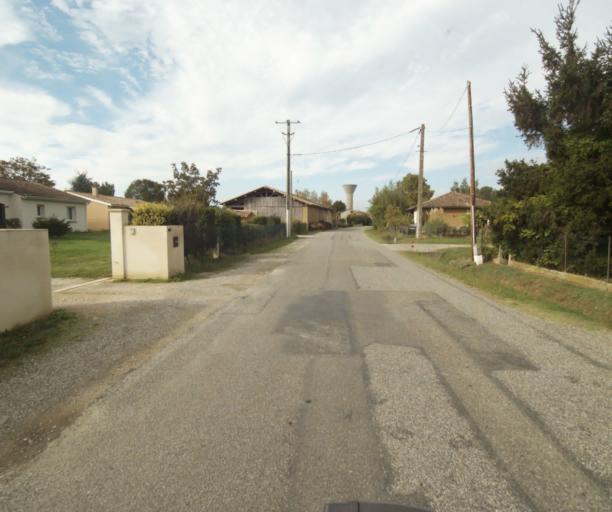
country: FR
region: Midi-Pyrenees
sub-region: Departement du Tarn-et-Garonne
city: Finhan
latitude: 43.9145
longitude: 1.2305
